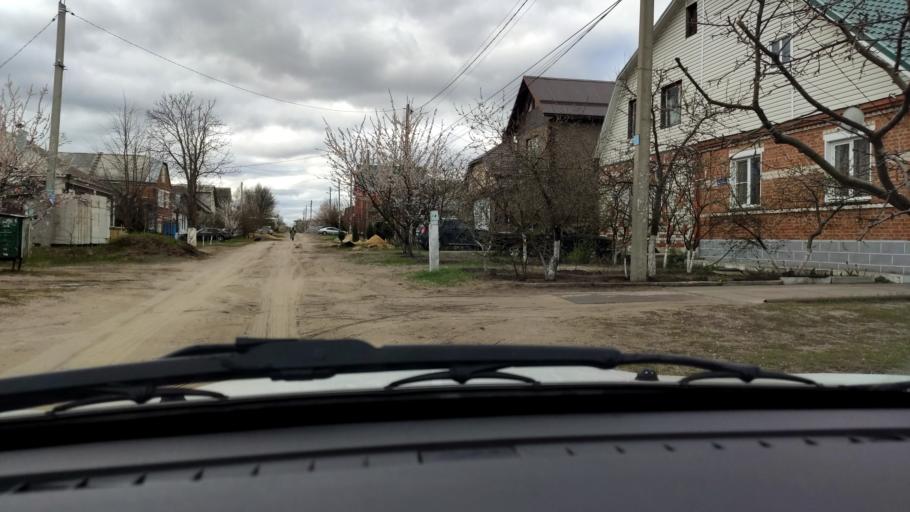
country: RU
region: Voronezj
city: Somovo
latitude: 51.7378
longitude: 39.2697
